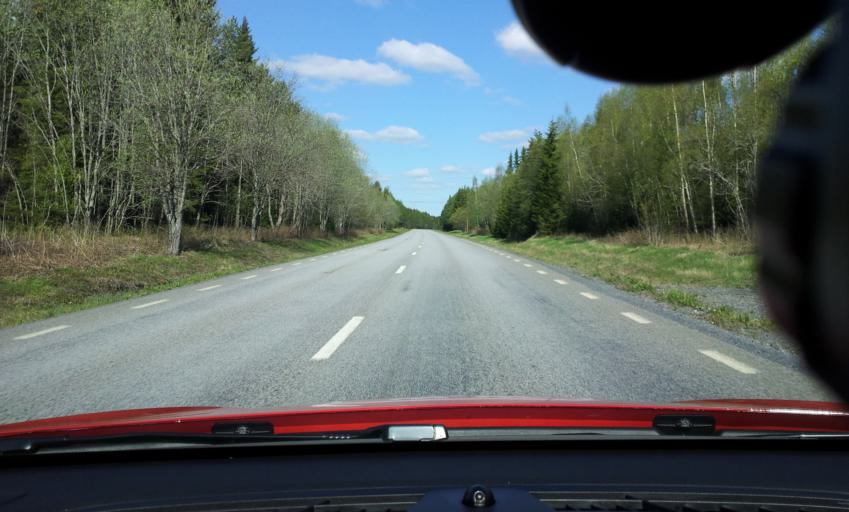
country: SE
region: Jaemtland
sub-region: Krokoms Kommun
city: Valla
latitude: 63.2698
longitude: 13.9561
